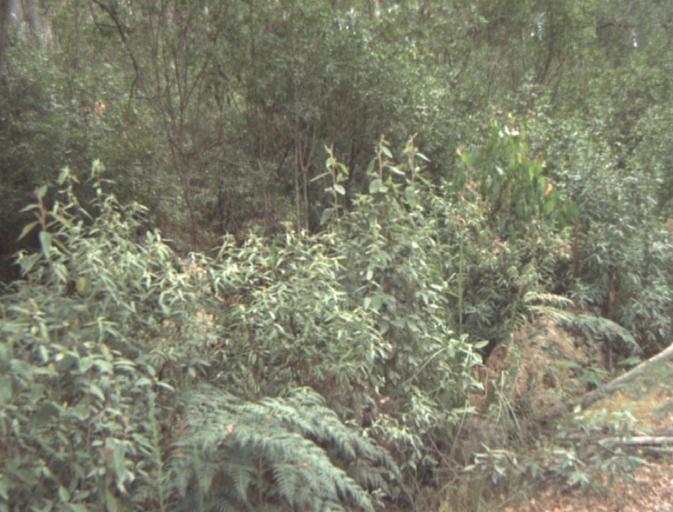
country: AU
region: Tasmania
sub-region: Launceston
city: Mayfield
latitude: -41.1937
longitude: 147.1602
